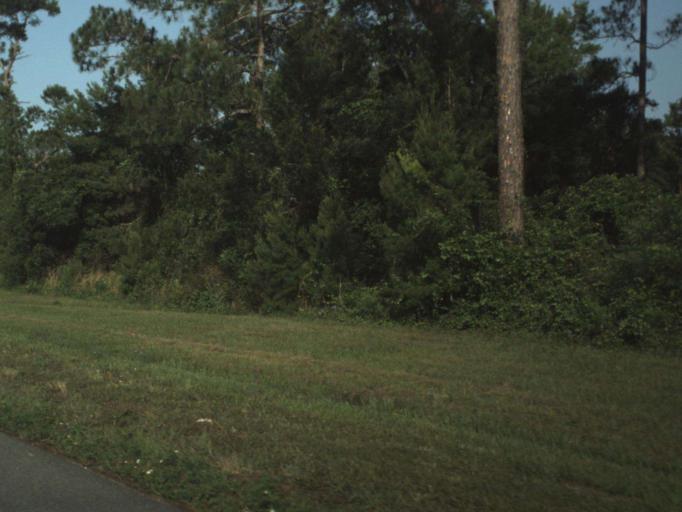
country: US
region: Florida
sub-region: Volusia County
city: North DeLand
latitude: 29.0706
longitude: -81.2535
